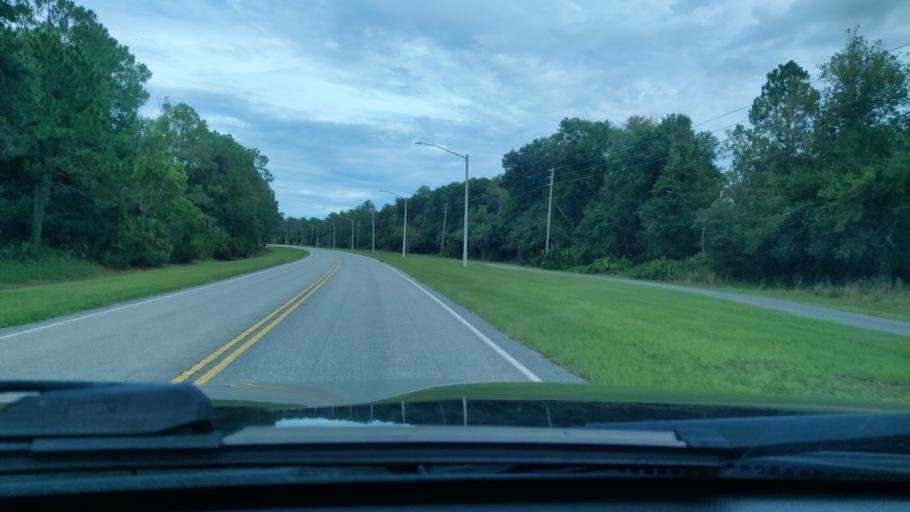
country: US
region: Florida
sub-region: Flagler County
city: Bunnell
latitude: 29.5291
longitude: -81.2499
